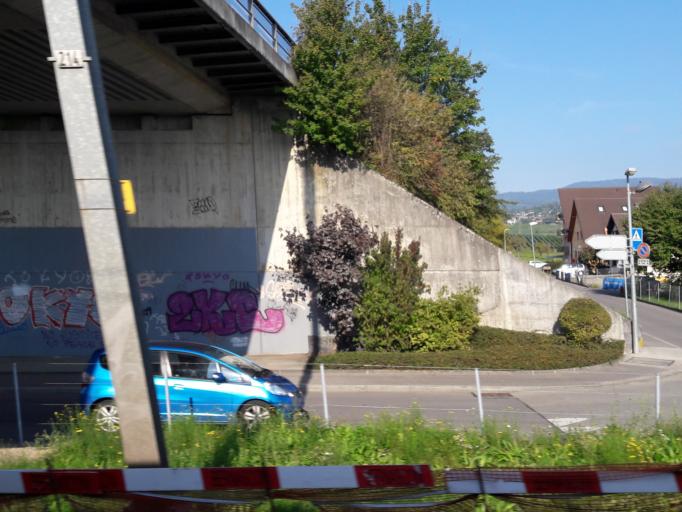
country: CH
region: Vaud
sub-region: Nyon District
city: Gland
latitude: 46.4241
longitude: 6.2735
